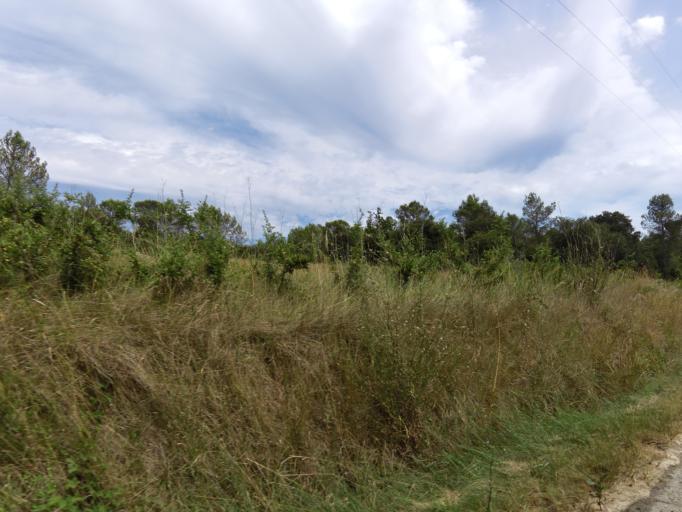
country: FR
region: Languedoc-Roussillon
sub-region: Departement du Gard
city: Congenies
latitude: 43.8147
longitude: 4.1481
